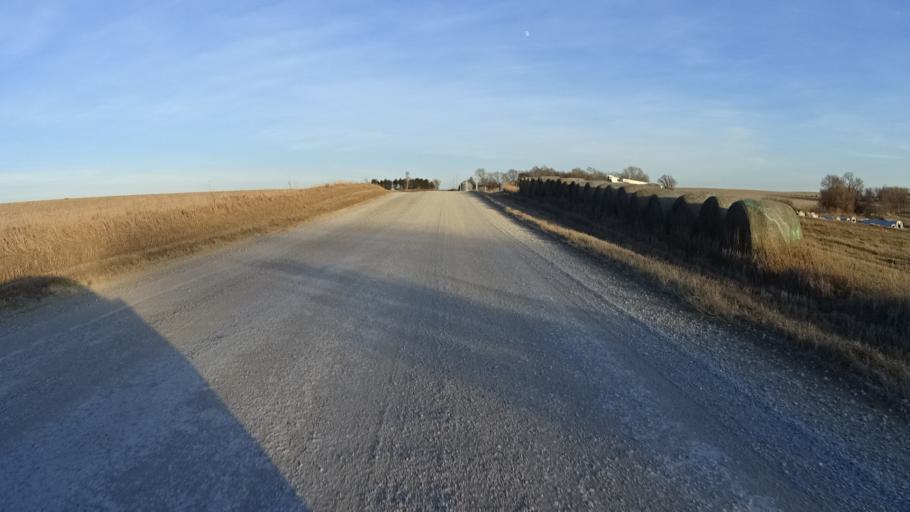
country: US
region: Nebraska
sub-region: Sarpy County
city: Springfield
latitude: 41.1326
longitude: -96.1124
